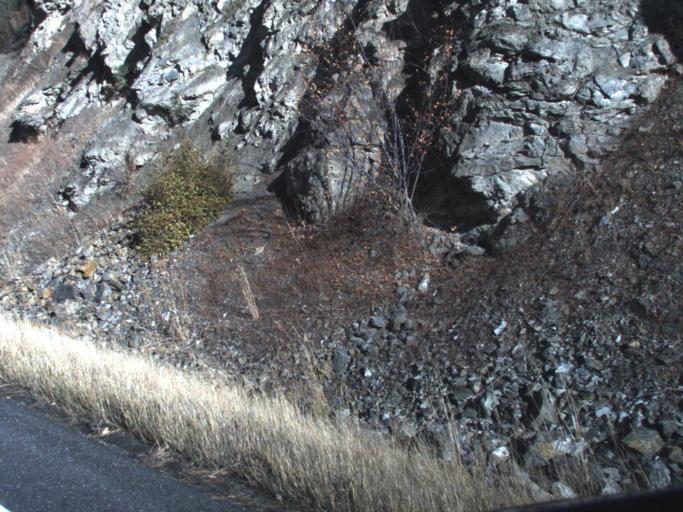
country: US
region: Washington
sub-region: Stevens County
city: Kettle Falls
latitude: 48.6573
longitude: -118.0849
